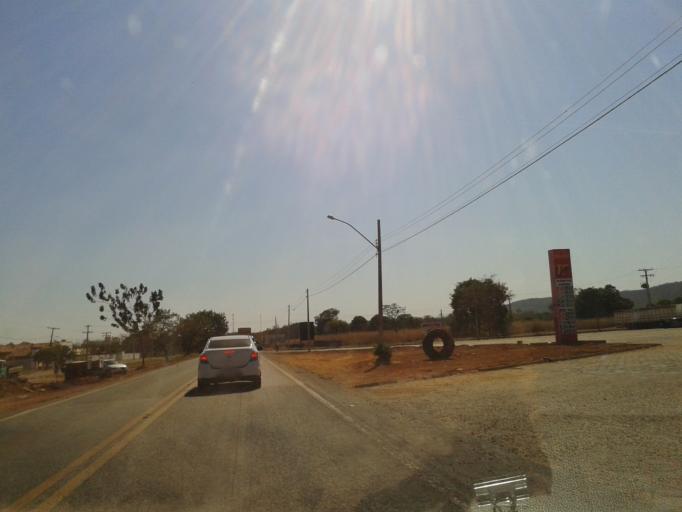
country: BR
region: Goias
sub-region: Crixas
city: Crixas
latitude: -14.1107
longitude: -50.3422
